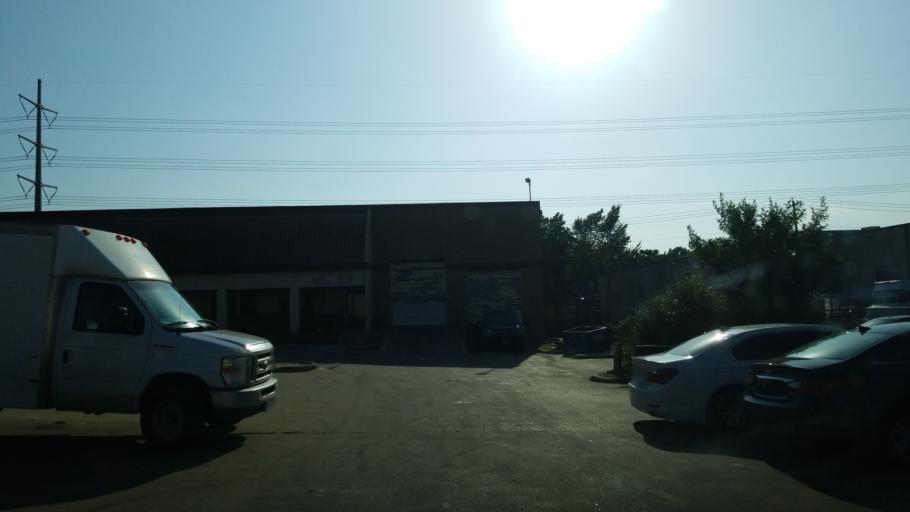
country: US
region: Texas
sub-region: Dallas County
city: Farmers Branch
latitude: 32.8793
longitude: -96.8909
